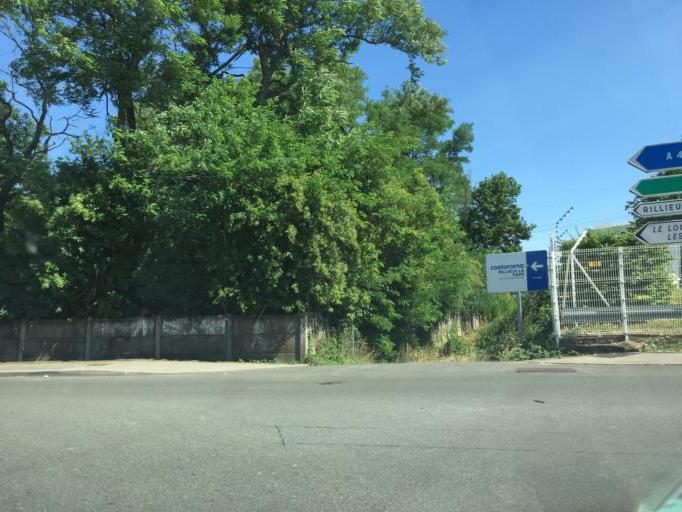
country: FR
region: Rhone-Alpes
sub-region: Departement du Rhone
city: Sathonay-Camp
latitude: 45.8128
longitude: 4.8806
